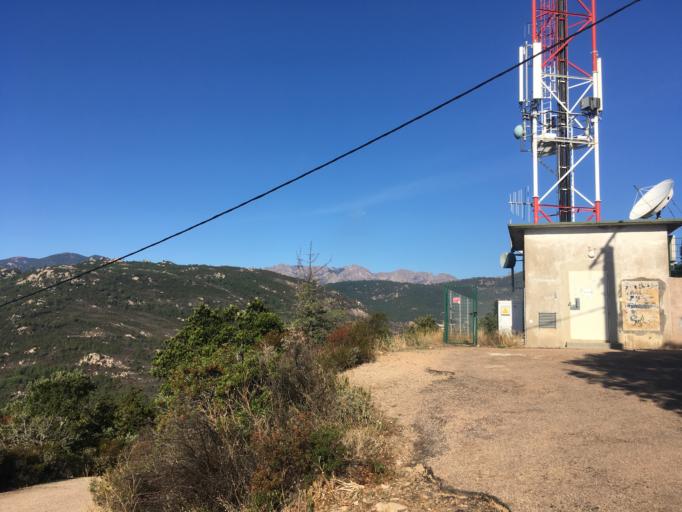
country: FR
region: Corsica
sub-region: Departement de la Corse-du-Sud
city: Sari-Solenzara
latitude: 41.7197
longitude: 9.3524
